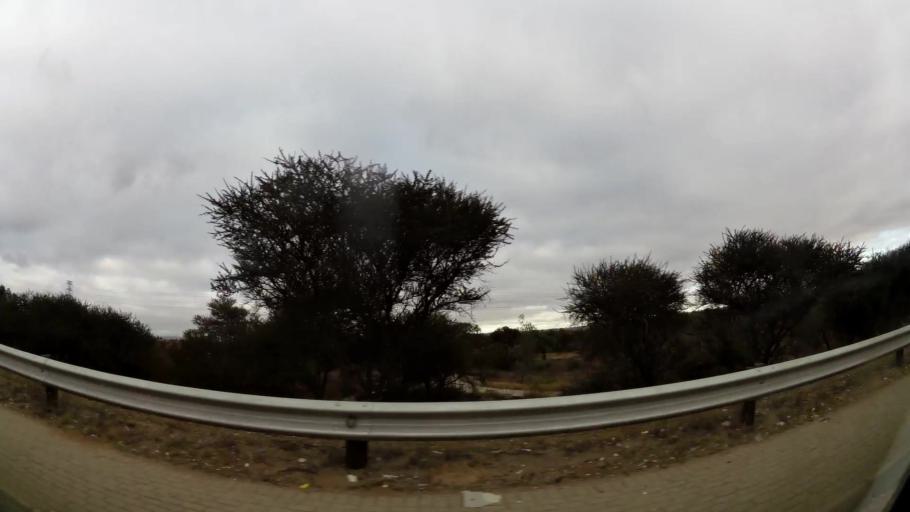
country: ZA
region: Limpopo
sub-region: Capricorn District Municipality
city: Polokwane
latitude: -23.9009
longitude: 29.4402
